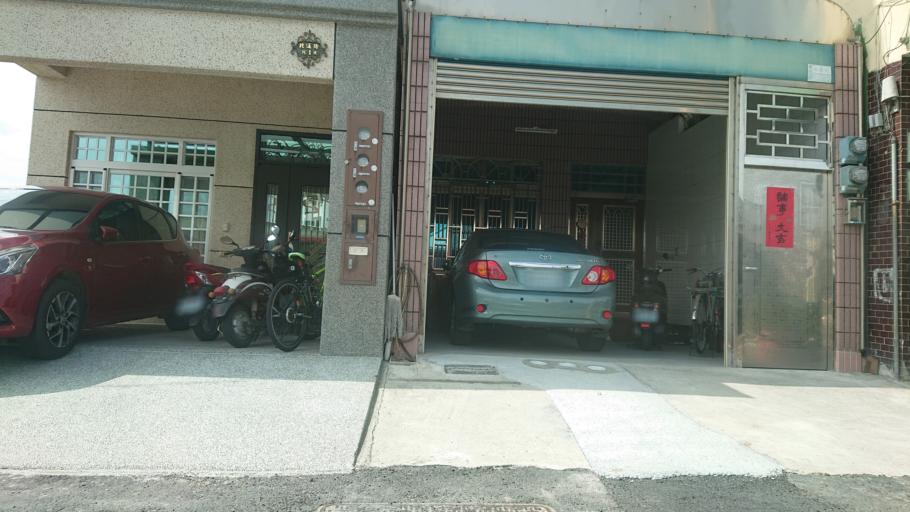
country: TW
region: Taiwan
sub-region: Chiayi
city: Taibao
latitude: 23.4708
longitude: 120.2446
